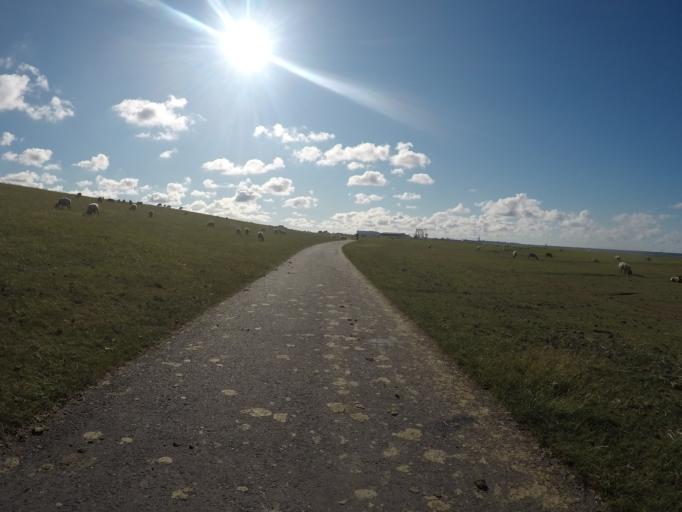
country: DE
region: Lower Saxony
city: Nordleda
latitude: 53.8330
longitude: 8.7892
